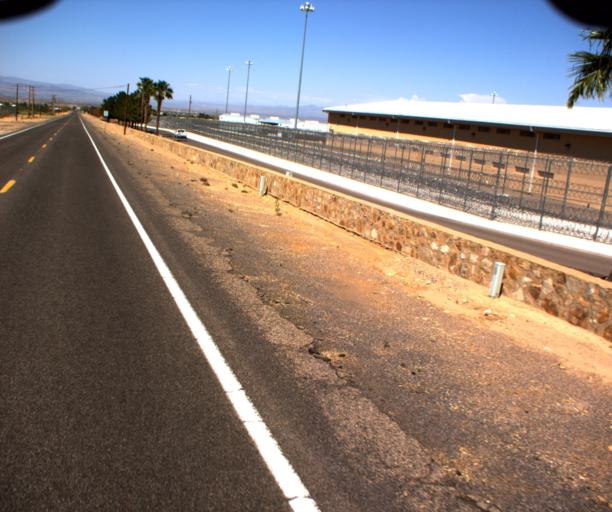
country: US
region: Arizona
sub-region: Graham County
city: Swift Trail Junction
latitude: 32.7179
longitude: -109.7263
